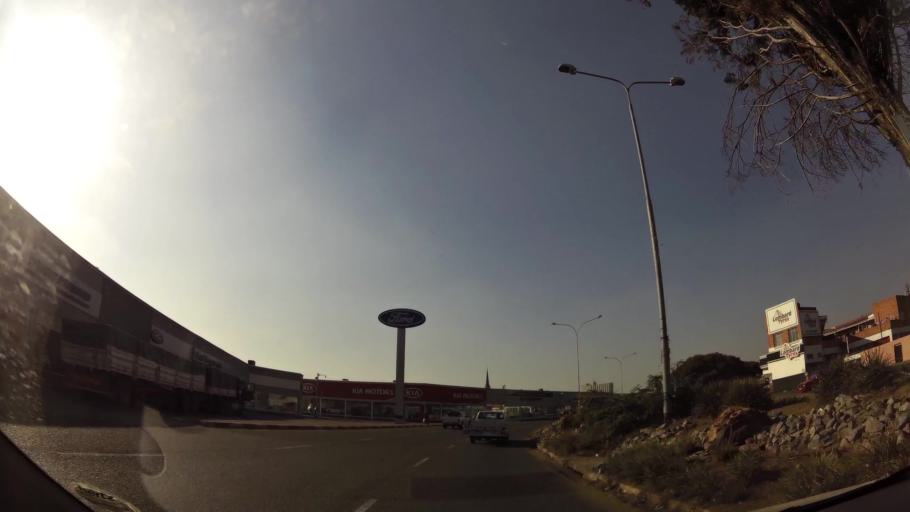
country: ZA
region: Gauteng
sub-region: West Rand District Municipality
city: Randfontein
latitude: -26.1752
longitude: 27.7054
